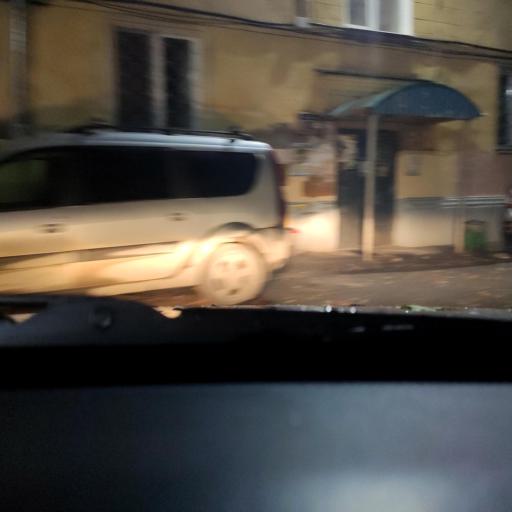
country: RU
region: Perm
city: Kultayevo
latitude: 58.0020
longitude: 55.9502
